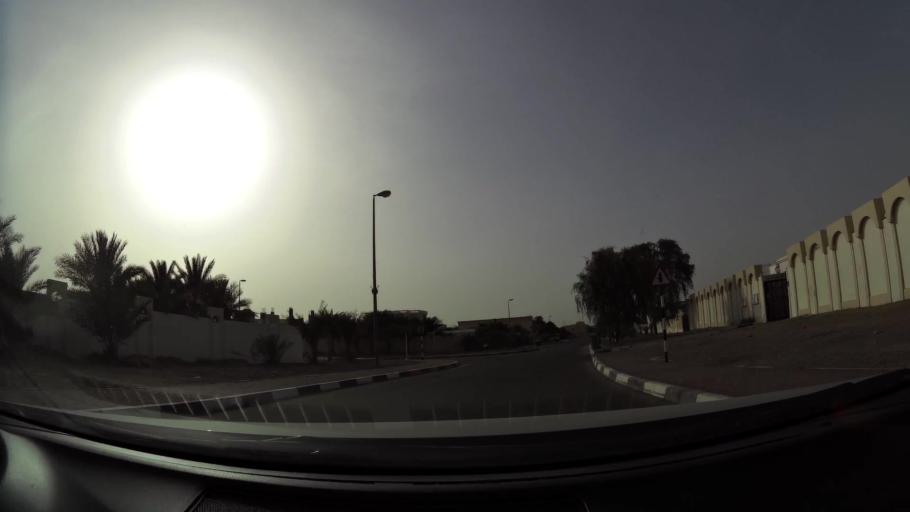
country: AE
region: Abu Dhabi
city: Al Ain
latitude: 24.2225
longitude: 55.6680
